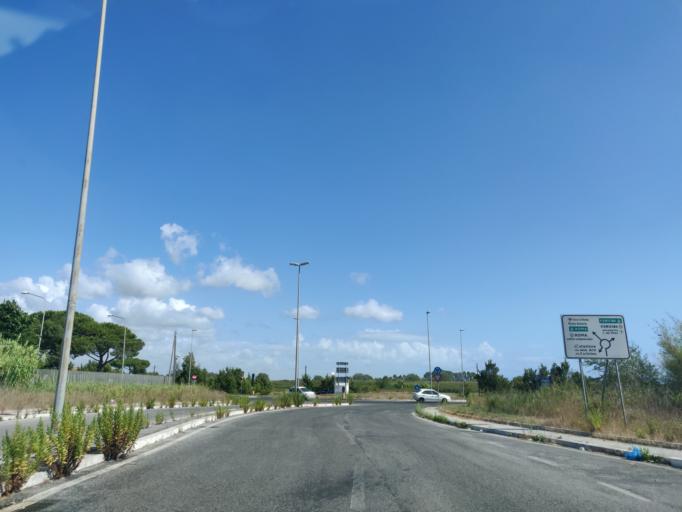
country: IT
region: Latium
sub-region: Citta metropolitana di Roma Capitale
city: Npp 23 (Parco Leonardo)
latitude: 41.7939
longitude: 12.2917
